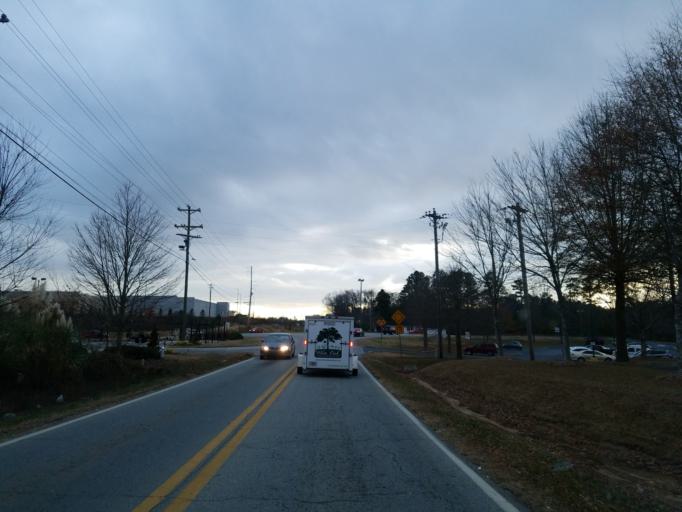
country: US
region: Georgia
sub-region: Dawson County
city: Dawsonville
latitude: 34.3552
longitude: -84.0509
